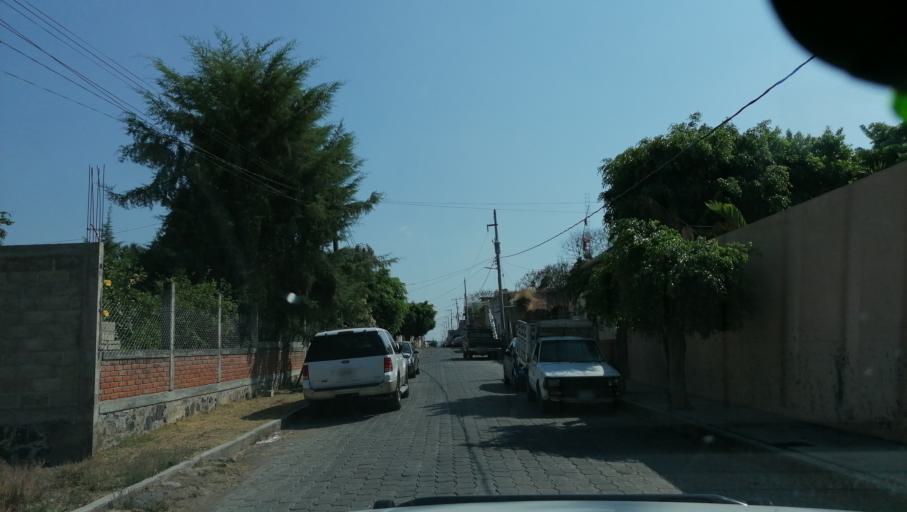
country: MX
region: Puebla
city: Huaquechula
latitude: 18.7718
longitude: -98.5392
